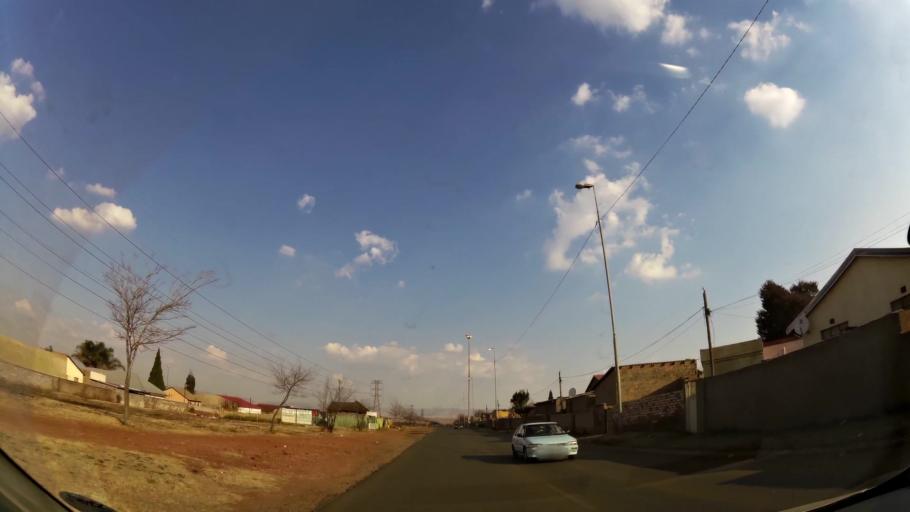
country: ZA
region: Gauteng
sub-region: Ekurhuleni Metropolitan Municipality
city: Germiston
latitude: -26.3585
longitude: 28.2281
